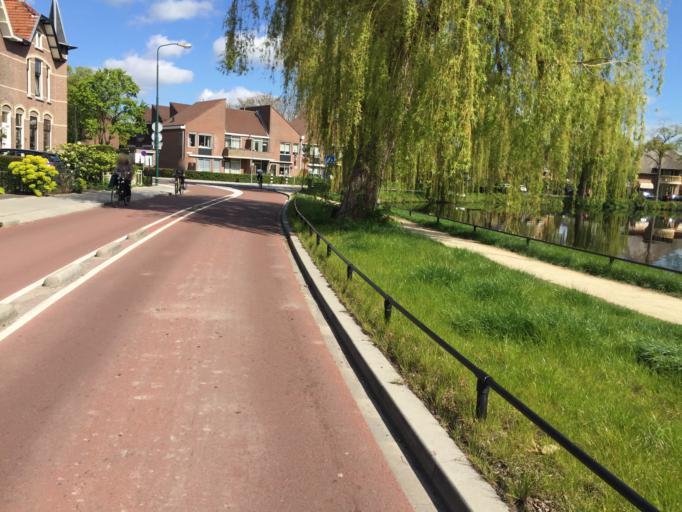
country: NL
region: Utrecht
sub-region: Gemeente Woerden
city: Woerden
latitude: 52.0884
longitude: 4.8804
